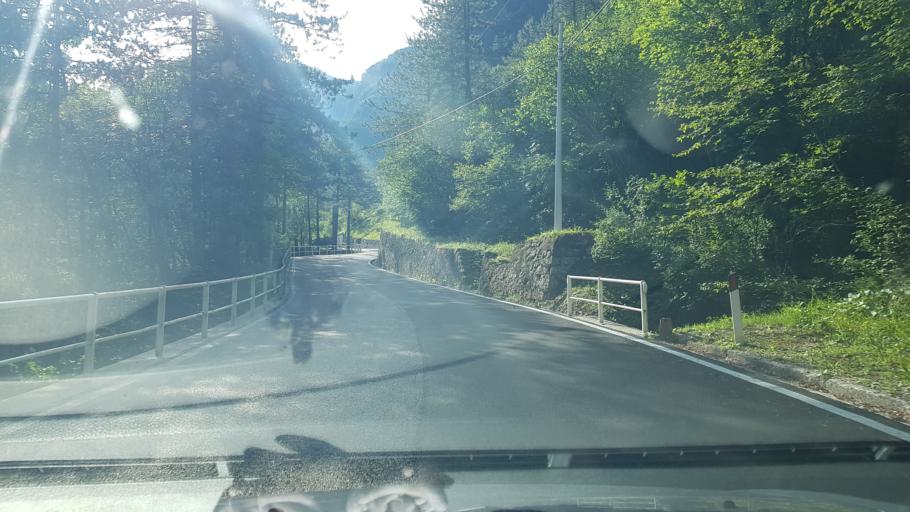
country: IT
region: Friuli Venezia Giulia
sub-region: Provincia di Udine
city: Chiusaforte
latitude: 46.4000
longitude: 13.3194
